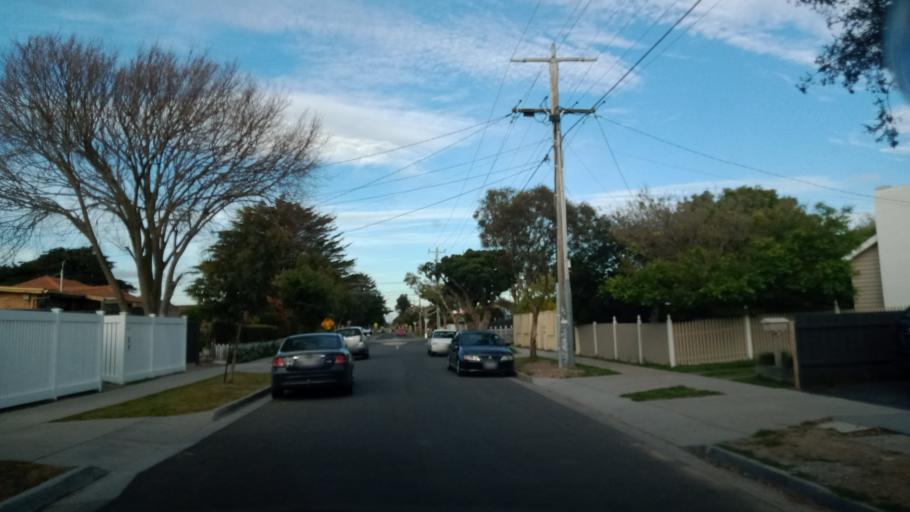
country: AU
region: Victoria
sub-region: Kingston
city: Edithvale
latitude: -38.0381
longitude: 145.1175
